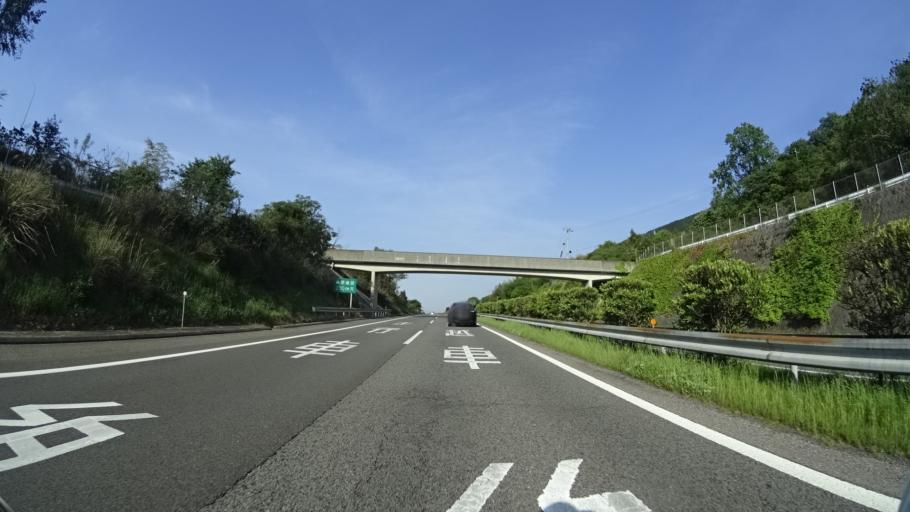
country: JP
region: Ehime
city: Niihama
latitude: 33.9147
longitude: 133.2807
